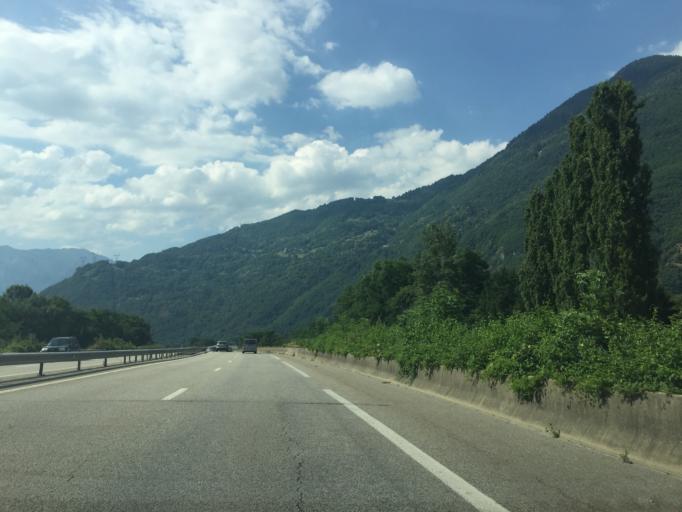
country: FR
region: Rhone-Alpes
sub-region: Departement de la Savoie
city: La Bathie
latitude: 45.6509
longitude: 6.4365
